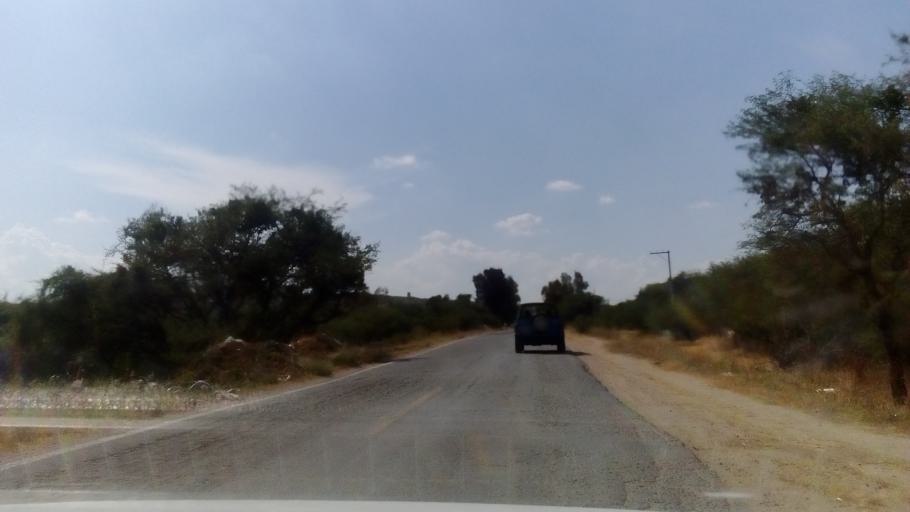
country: MX
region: Guanajuato
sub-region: Silao de la Victoria
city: San Francisco (Banos de Agua Caliente)
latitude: 21.0769
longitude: -101.4767
